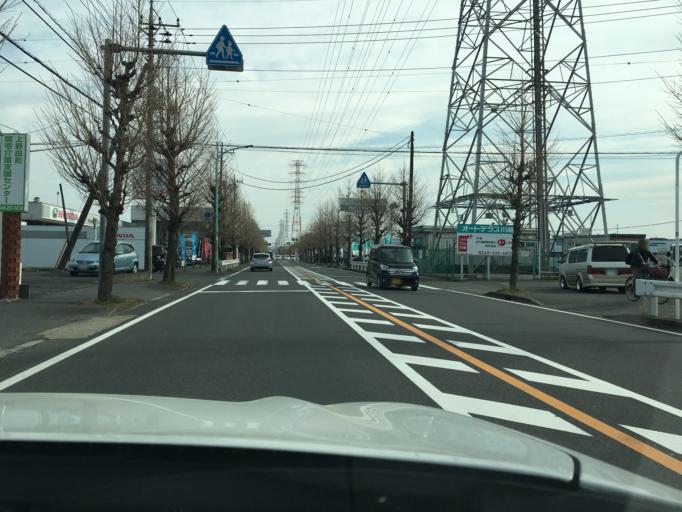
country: JP
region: Saitama
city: Kawagoe
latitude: 35.9128
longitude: 139.4690
